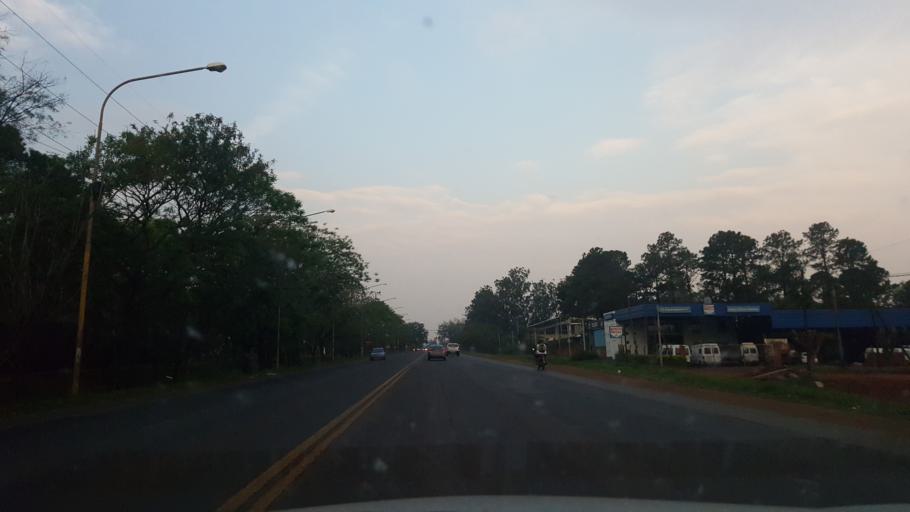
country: AR
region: Misiones
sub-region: Departamento de Capital
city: Posadas
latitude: -27.4004
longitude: -55.9397
